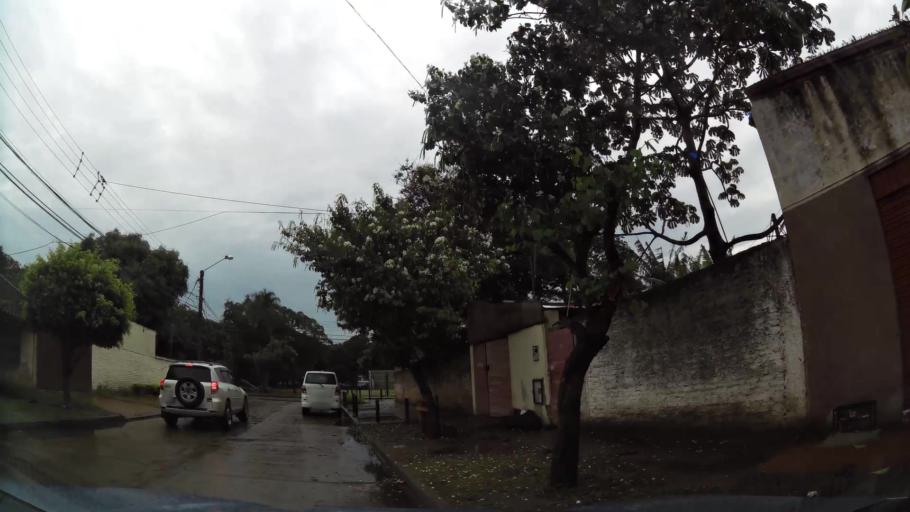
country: BO
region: Santa Cruz
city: Santa Cruz de la Sierra
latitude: -17.7929
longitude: -63.2114
